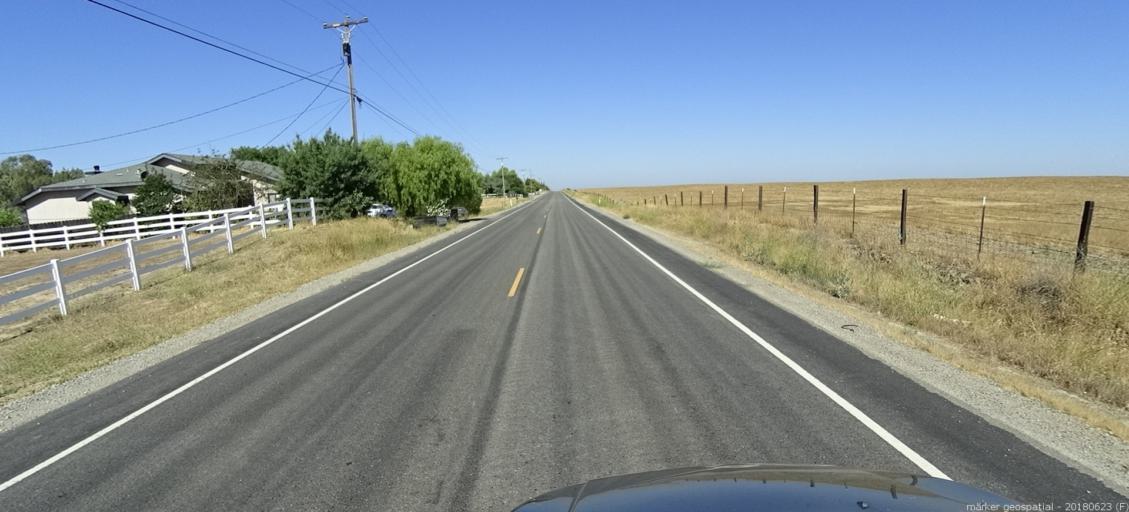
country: US
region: California
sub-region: Madera County
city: Bonadelle Ranchos-Madera Ranchos
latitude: 36.9666
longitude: -119.8971
